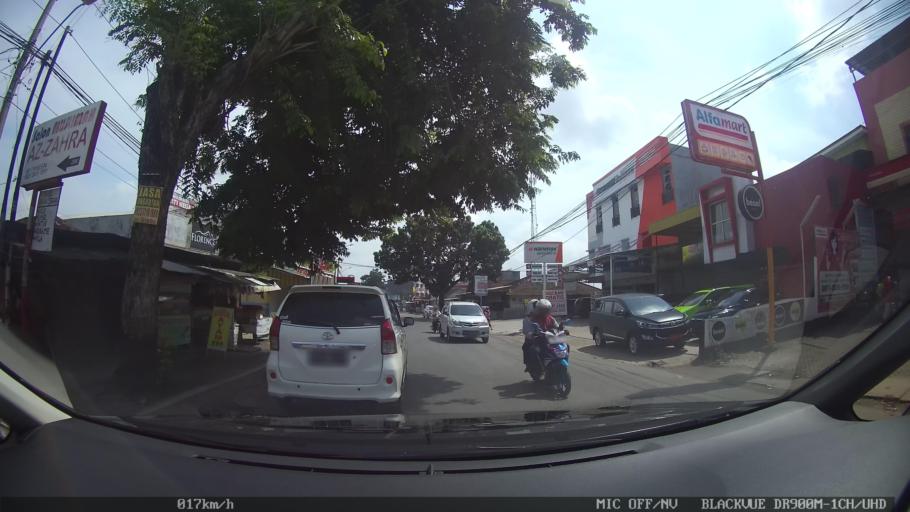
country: ID
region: Lampung
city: Kedaton
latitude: -5.3655
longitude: 105.2755
